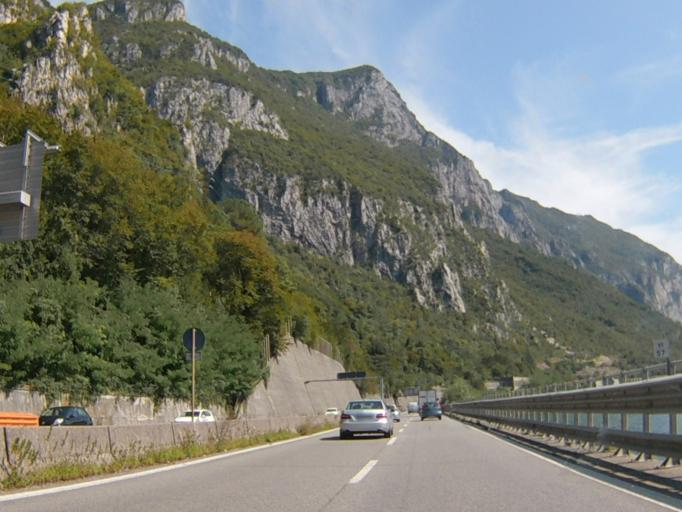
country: IT
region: Lombardy
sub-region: Provincia di Lecco
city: Abbadia Lariana
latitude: 45.8940
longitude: 9.3496
